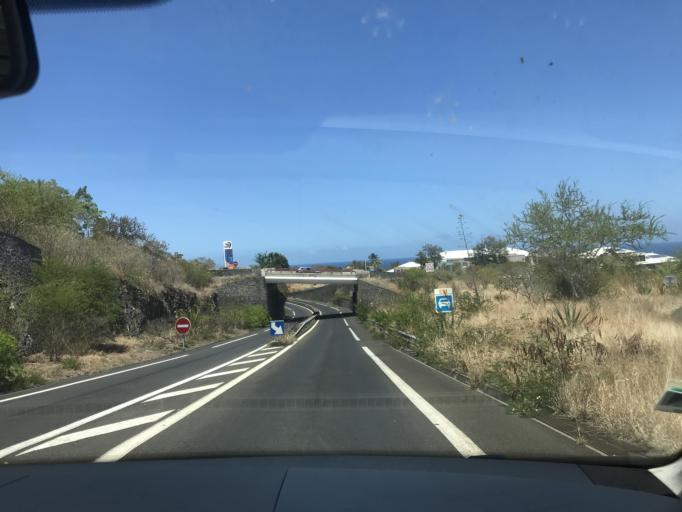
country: RE
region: Reunion
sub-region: Reunion
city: Saint-Paul
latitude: -21.0182
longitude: 55.2667
